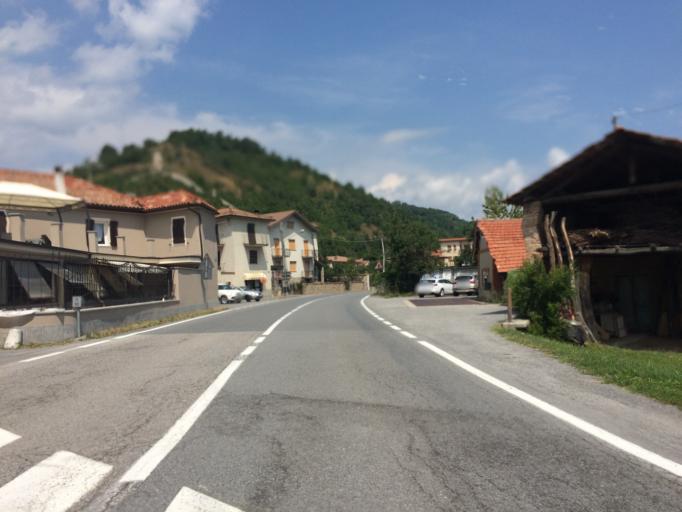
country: IT
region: Piedmont
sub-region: Provincia di Cuneo
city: Bagnasco
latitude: 44.3011
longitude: 8.0444
